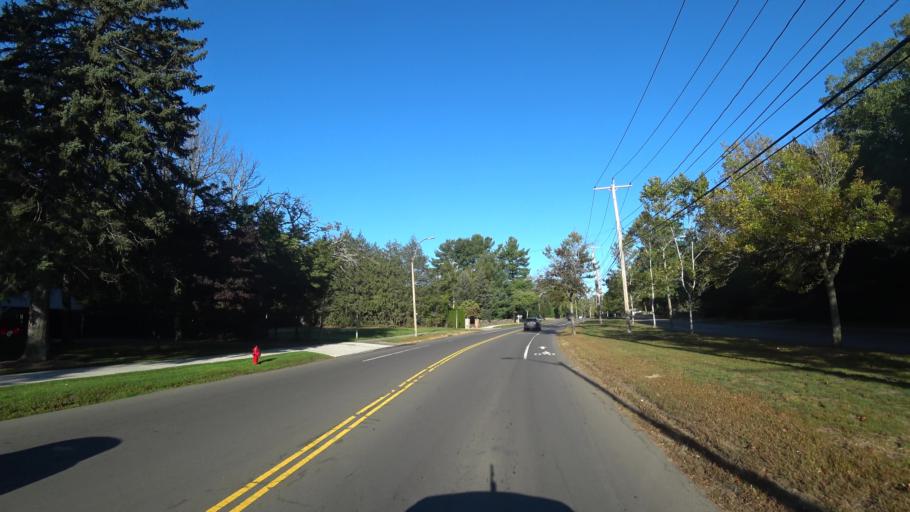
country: US
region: Massachusetts
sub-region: Middlesex County
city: Newton
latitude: 42.3370
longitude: -71.2246
